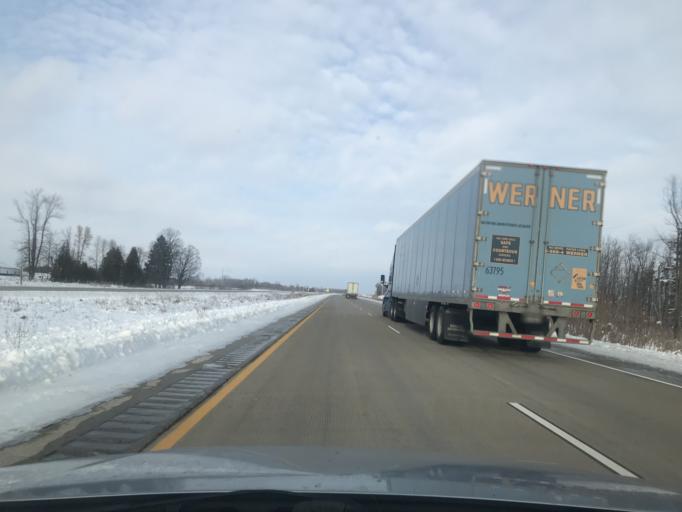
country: US
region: Wisconsin
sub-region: Oconto County
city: Oconto
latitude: 44.9992
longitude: -87.8524
